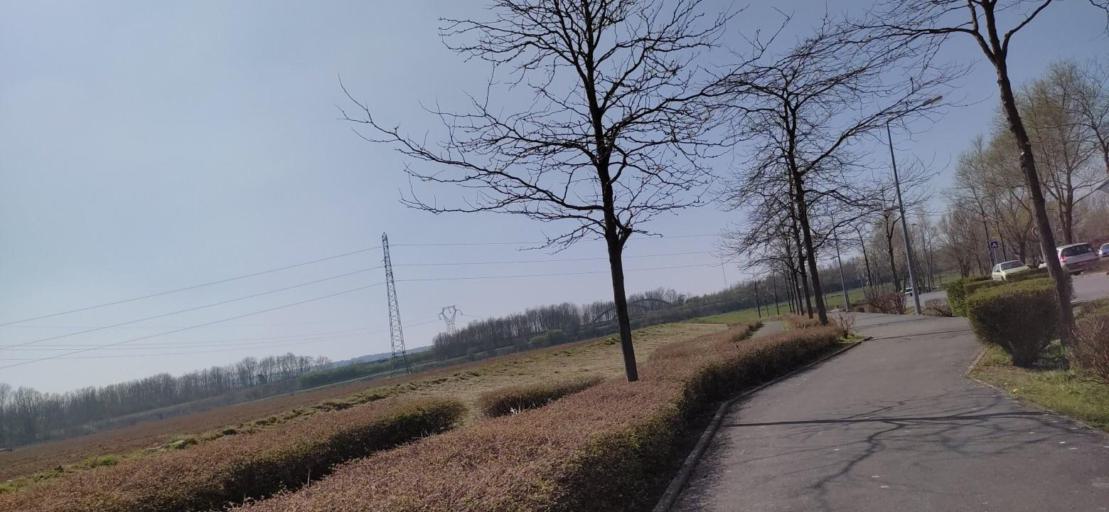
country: FR
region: Nord-Pas-de-Calais
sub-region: Departement du Pas-de-Calais
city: Aix-Noulette
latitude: 50.4368
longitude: 2.7137
